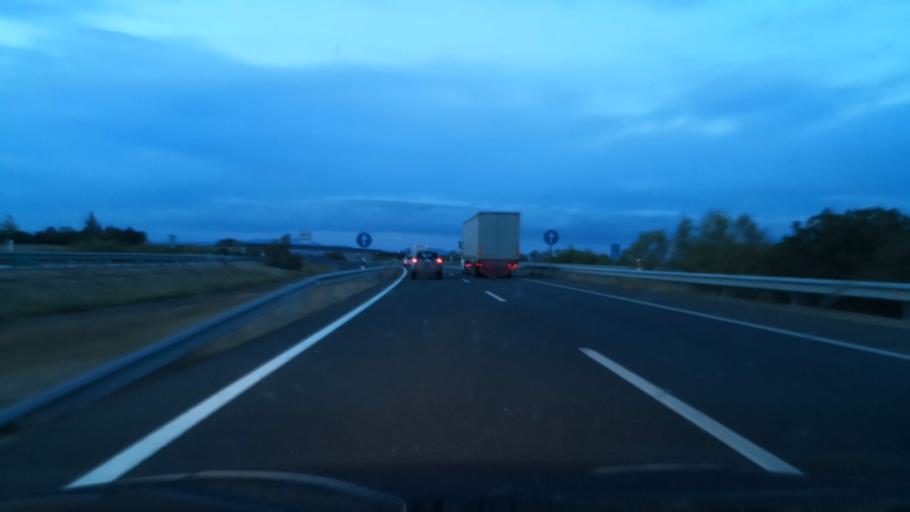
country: ES
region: Extremadura
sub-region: Provincia de Caceres
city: Casar de Caceres
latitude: 39.5578
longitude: -6.3999
